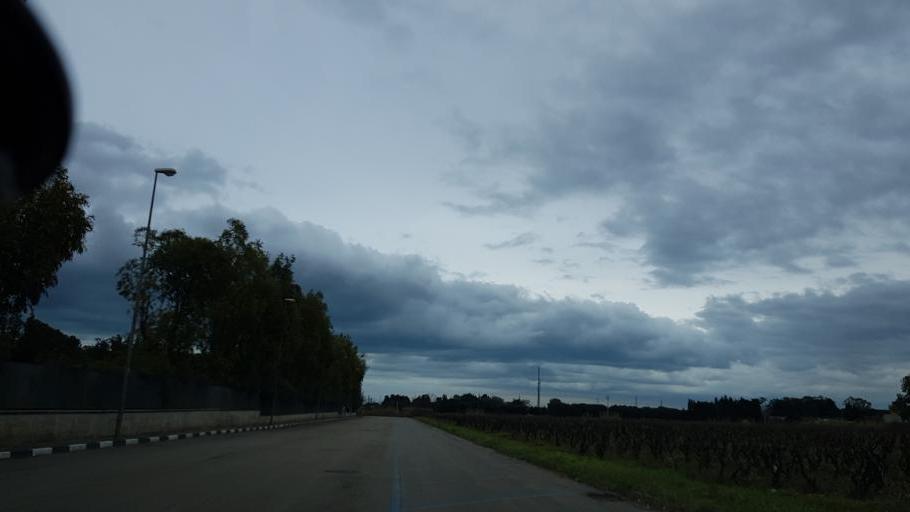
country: IT
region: Apulia
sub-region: Provincia di Brindisi
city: La Rosa
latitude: 40.6134
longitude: 17.9475
